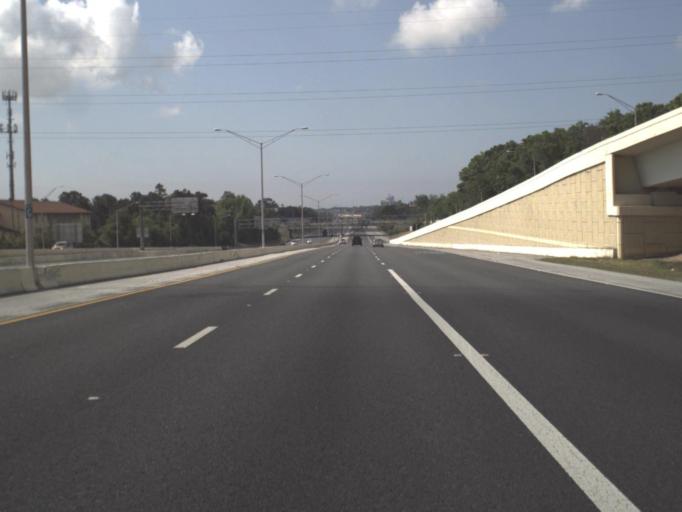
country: US
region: Florida
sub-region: Escambia County
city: Ferry Pass
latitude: 30.5012
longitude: -87.2301
